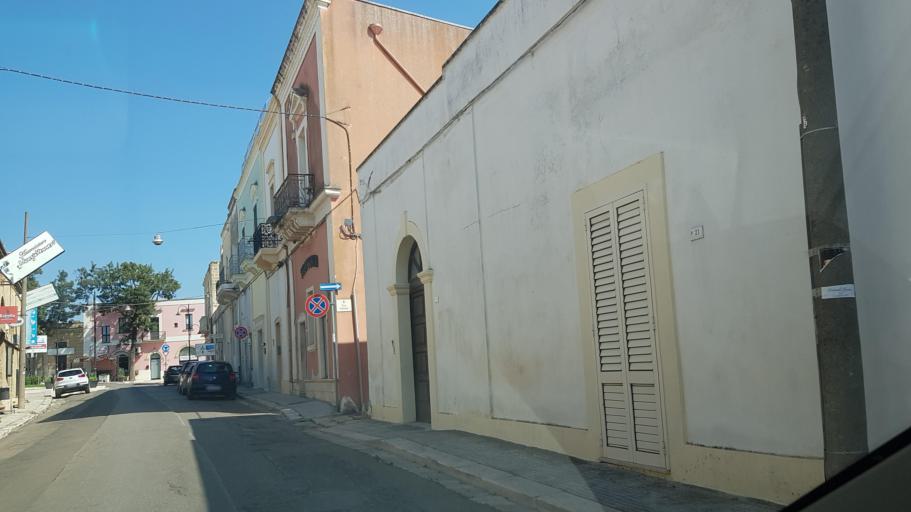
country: IT
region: Apulia
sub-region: Provincia di Lecce
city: Ugento
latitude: 39.9277
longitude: 18.1604
